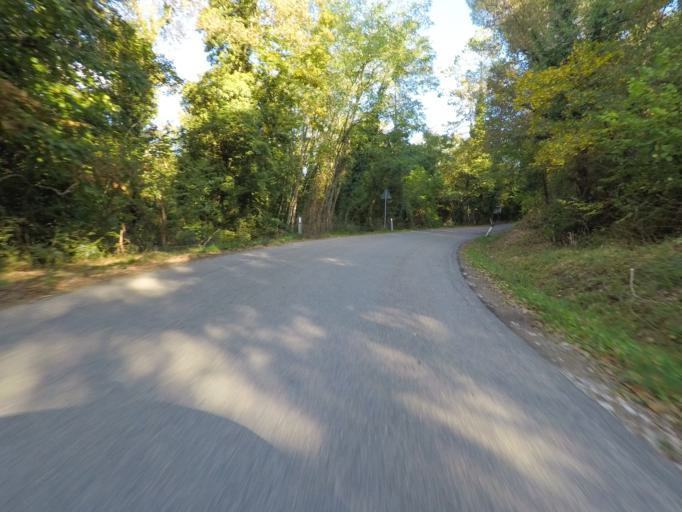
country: IT
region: Tuscany
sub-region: Provincia di Siena
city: Radda in Chianti
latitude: 43.4673
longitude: 11.3738
